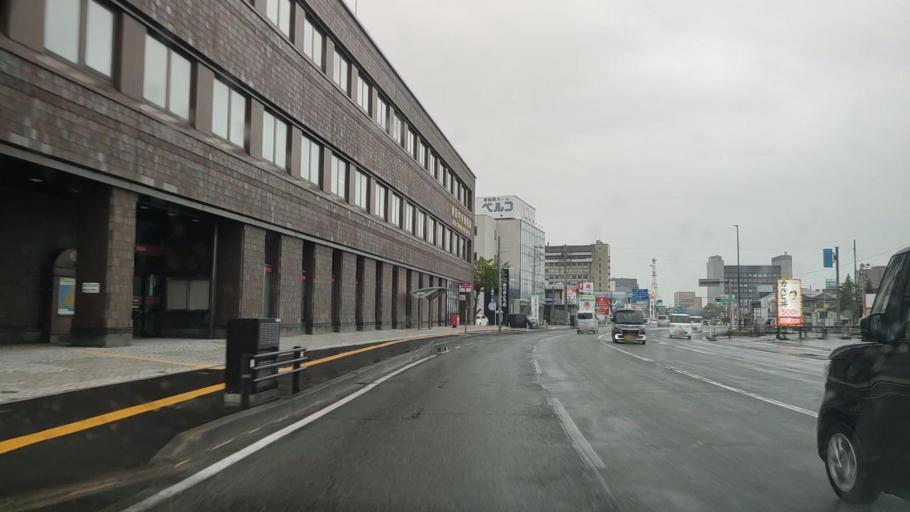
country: JP
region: Akita
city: Akita Shi
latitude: 39.7237
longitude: 140.1089
